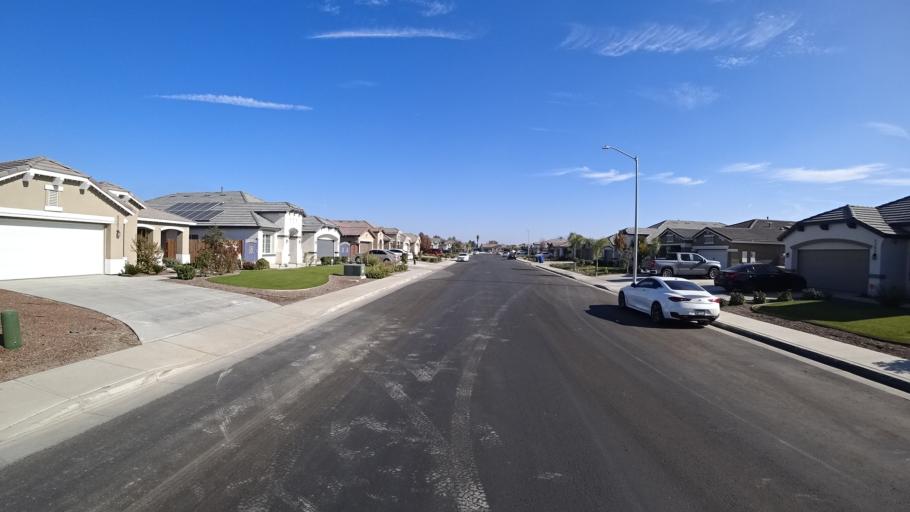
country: US
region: California
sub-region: Kern County
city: Greenfield
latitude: 35.2918
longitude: -119.0614
